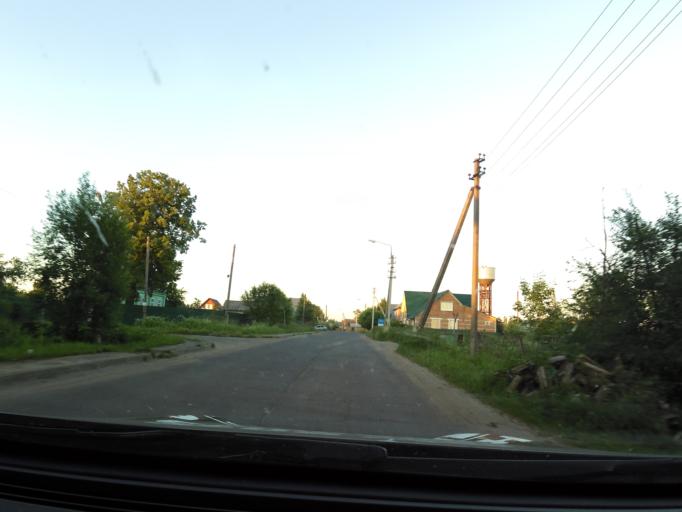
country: RU
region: Jaroslavl
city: Lyubim
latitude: 58.3553
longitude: 40.6839
